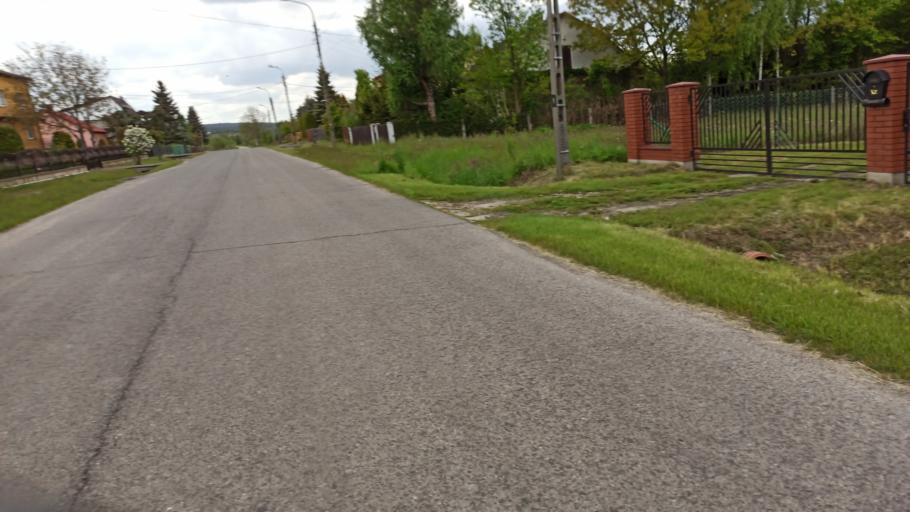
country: PL
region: Swietokrzyskie
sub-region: Powiat skarzyski
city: Skarzysko Koscielne
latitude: 51.1382
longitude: 20.9073
